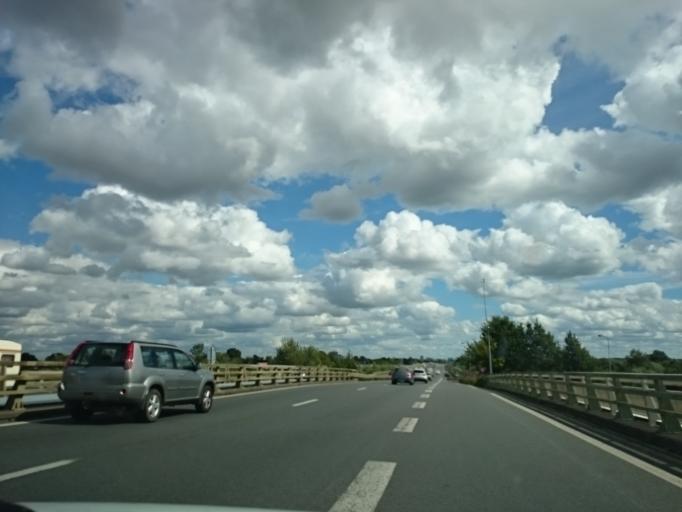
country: FR
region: Pays de la Loire
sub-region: Departement de la Loire-Atlantique
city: Sainte-Luce-sur-Loire
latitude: 47.2368
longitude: -1.4809
